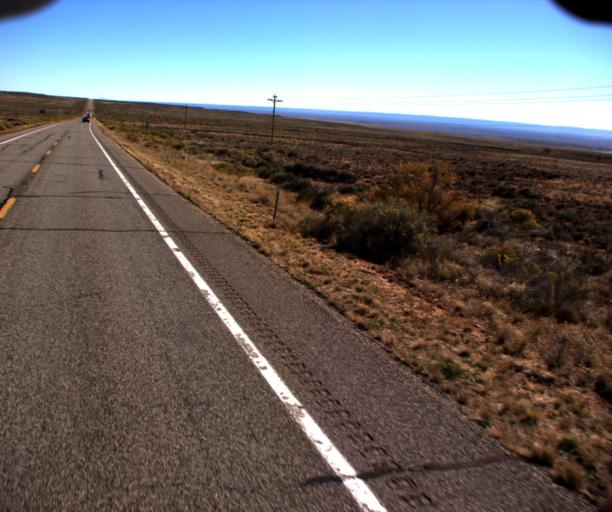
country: US
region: Arizona
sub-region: Coconino County
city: Fredonia
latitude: 36.8646
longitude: -112.7052
